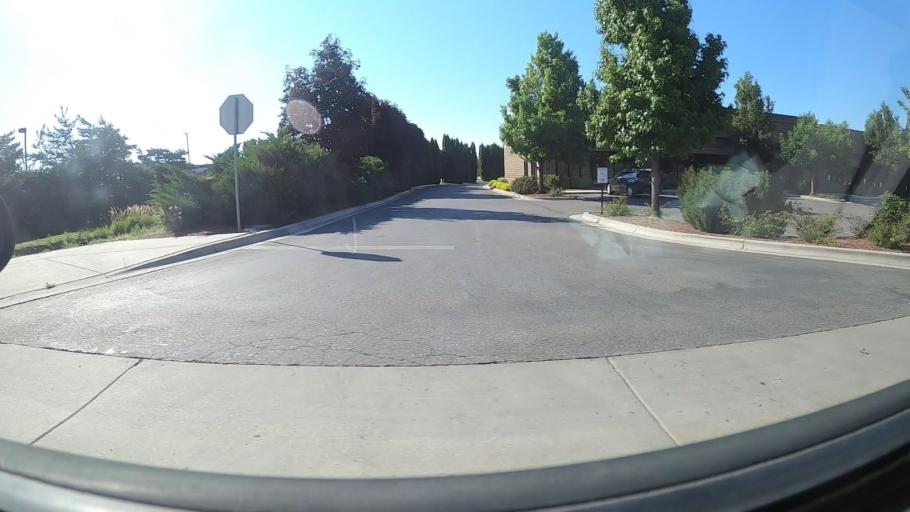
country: US
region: Idaho
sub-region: Ada County
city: Meridian
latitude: 43.5955
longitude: -116.3879
